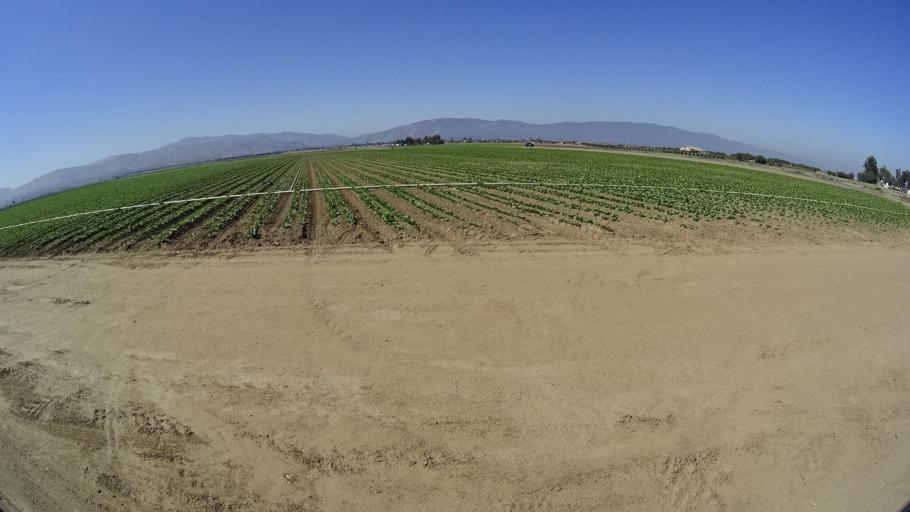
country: US
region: California
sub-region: Monterey County
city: Greenfield
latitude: 36.3332
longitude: -121.2115
